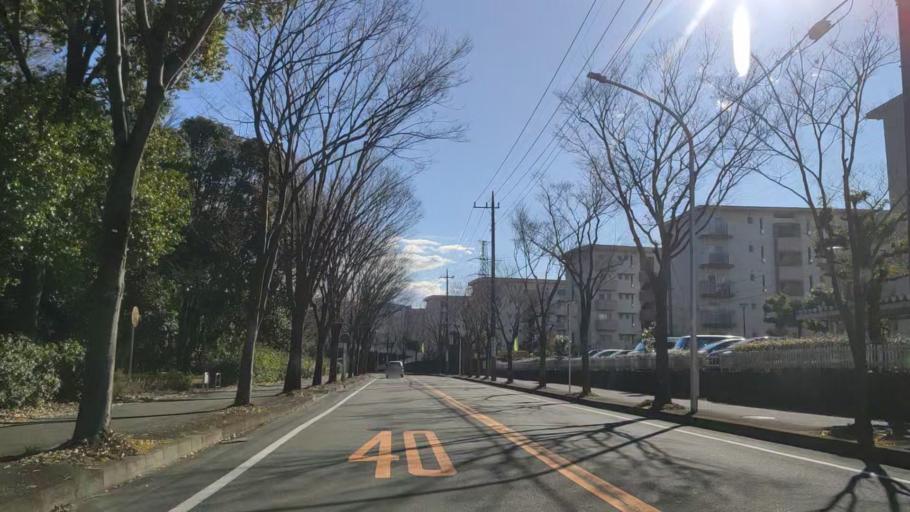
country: JP
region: Tokyo
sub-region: Machida-shi
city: Machida
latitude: 35.5140
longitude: 139.5006
